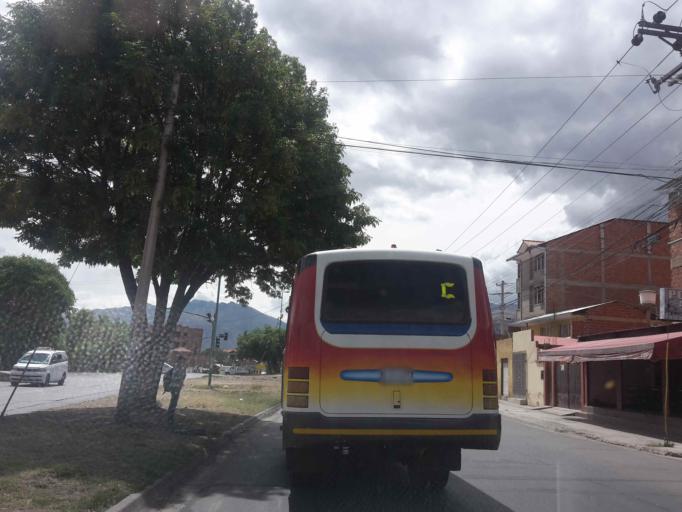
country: BO
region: Cochabamba
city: Cochabamba
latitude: -17.3587
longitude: -66.1746
